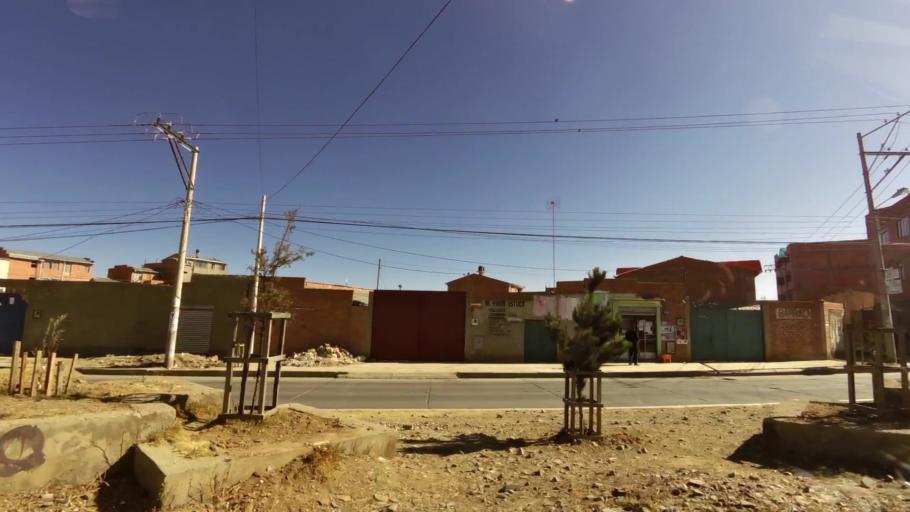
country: BO
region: La Paz
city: La Paz
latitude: -16.5329
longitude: -68.2147
